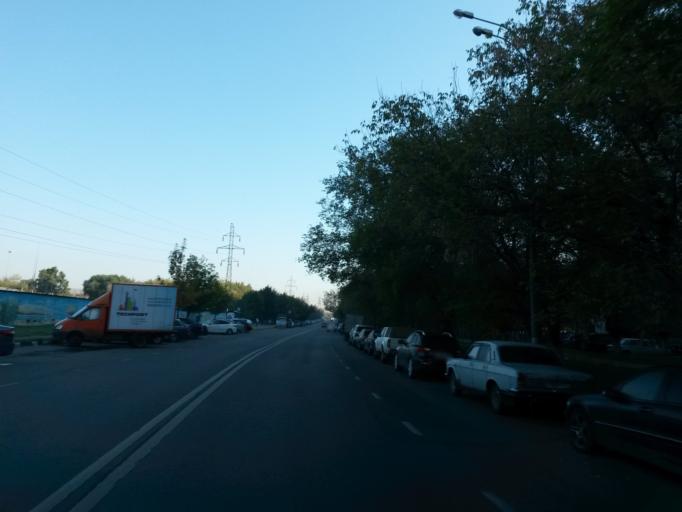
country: RU
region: Moskovskaya
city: Kur'yanovo
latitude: 55.6506
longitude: 37.7083
